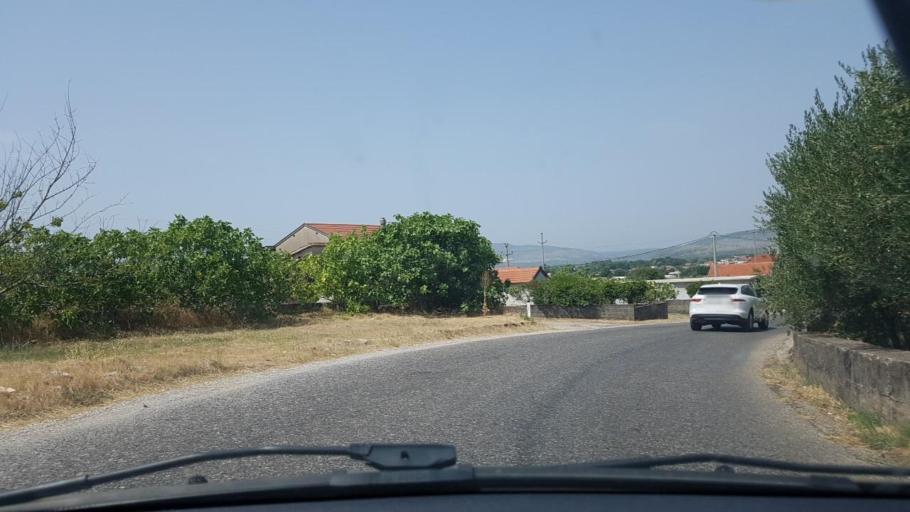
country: HR
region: Dubrovacko-Neretvanska
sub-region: Grad Dubrovnik
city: Metkovic
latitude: 43.0503
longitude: 17.7009
